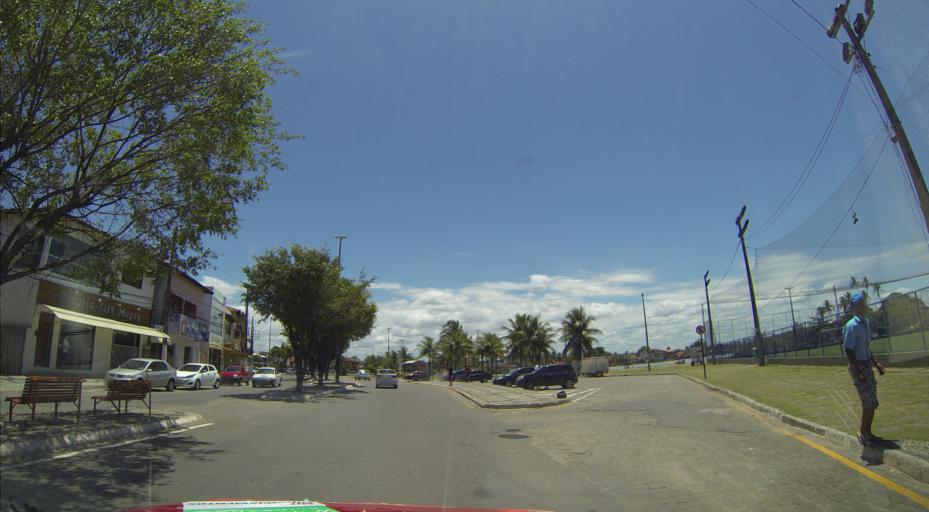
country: BR
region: Espirito Santo
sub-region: Serra
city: Serra
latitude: -20.0566
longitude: -40.1930
